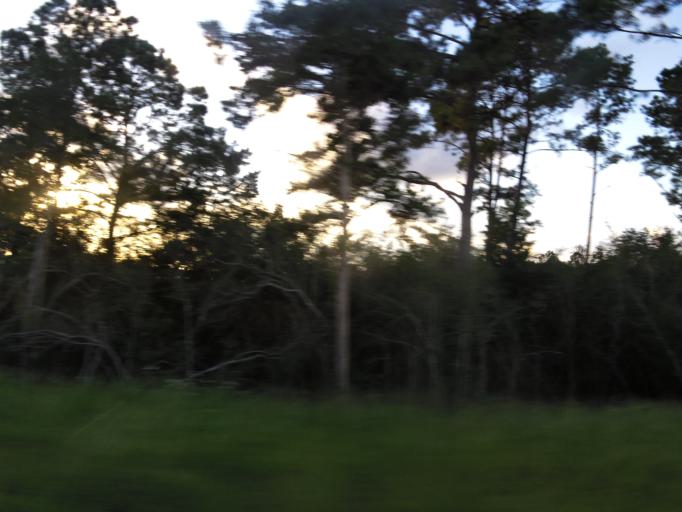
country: US
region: Georgia
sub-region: Glynn County
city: Brunswick
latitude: 31.1158
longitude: -81.6125
